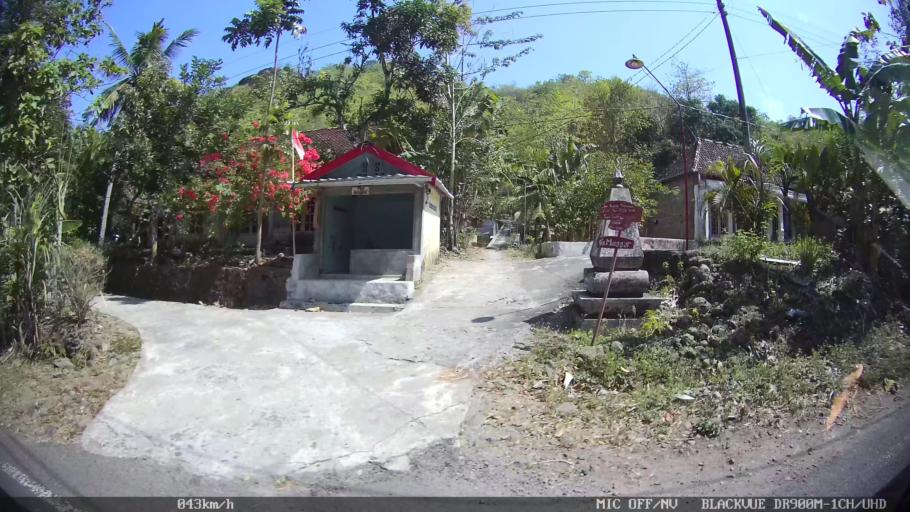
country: ID
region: Daerah Istimewa Yogyakarta
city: Pundong
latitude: -7.9599
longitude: 110.3763
